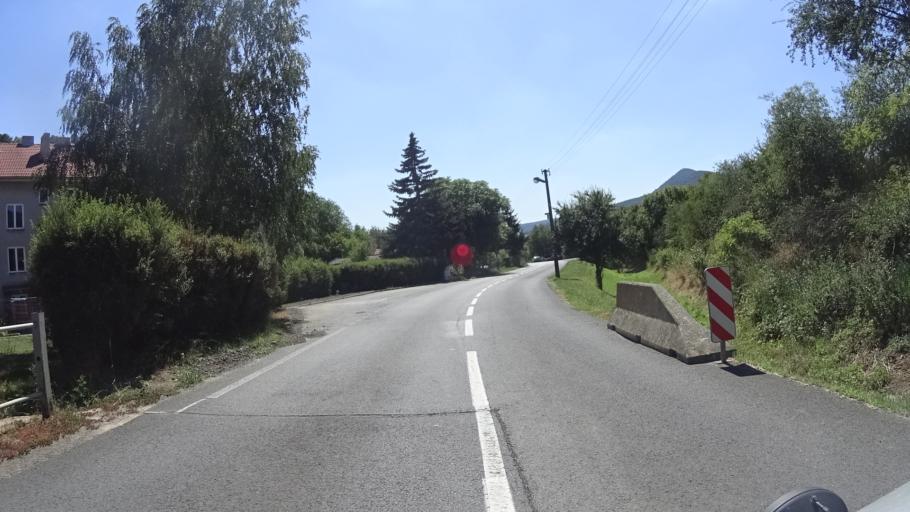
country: CZ
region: Ustecky
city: Lovosice
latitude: 50.5432
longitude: 14.0674
